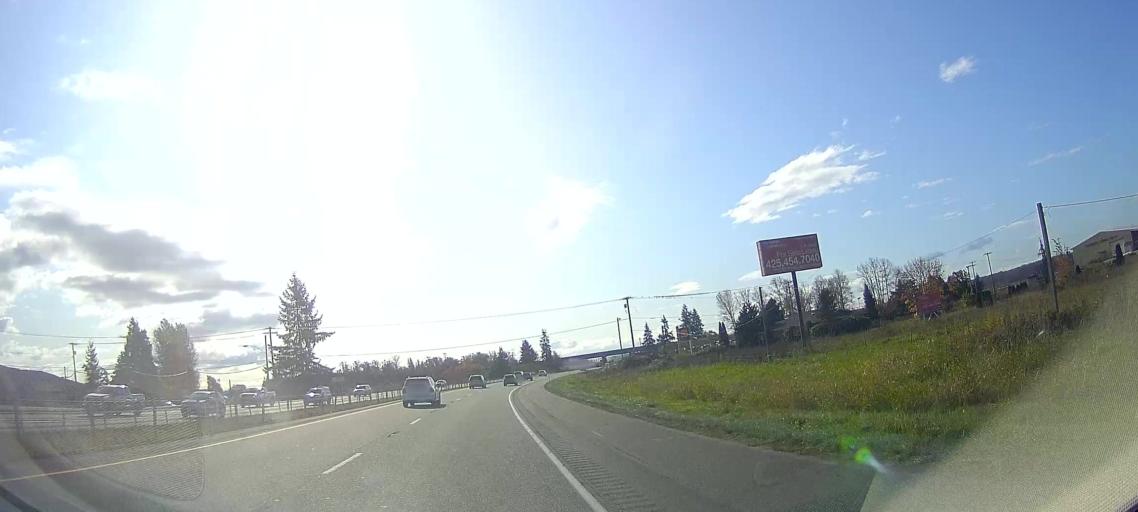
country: US
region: Washington
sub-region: Skagit County
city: Mount Vernon
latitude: 48.3857
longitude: -122.3312
